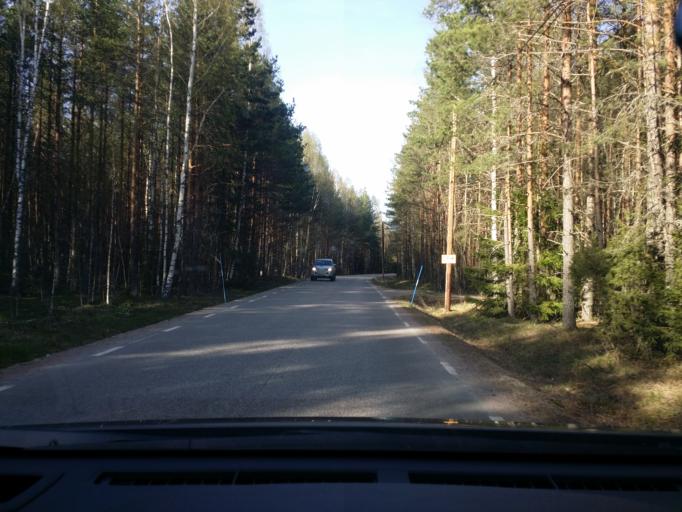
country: SE
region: Dalarna
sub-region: Avesta Kommun
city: Avesta
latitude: 60.0664
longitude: 16.3450
